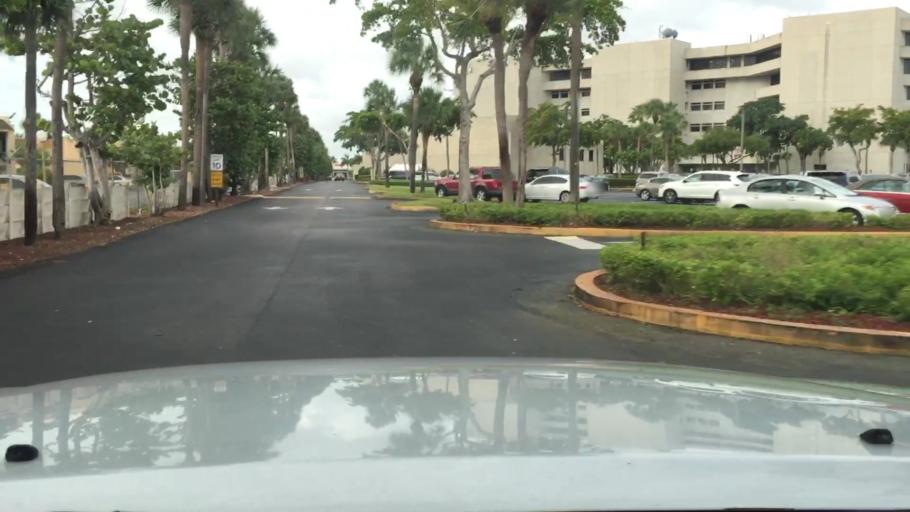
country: US
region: Florida
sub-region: Miami-Dade County
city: Fountainebleau
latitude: 25.7661
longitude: -80.3465
